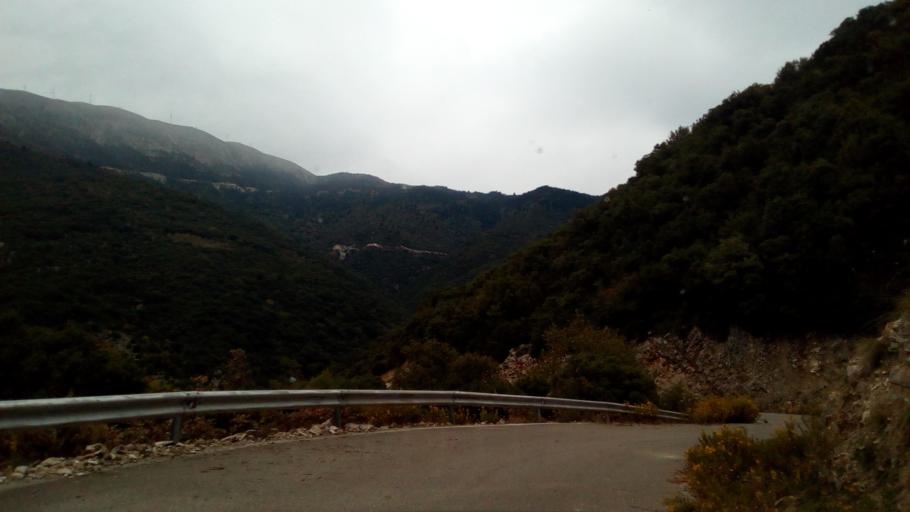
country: GR
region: West Greece
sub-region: Nomos Aitolias kai Akarnanias
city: Thermo
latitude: 38.6020
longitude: 21.8435
